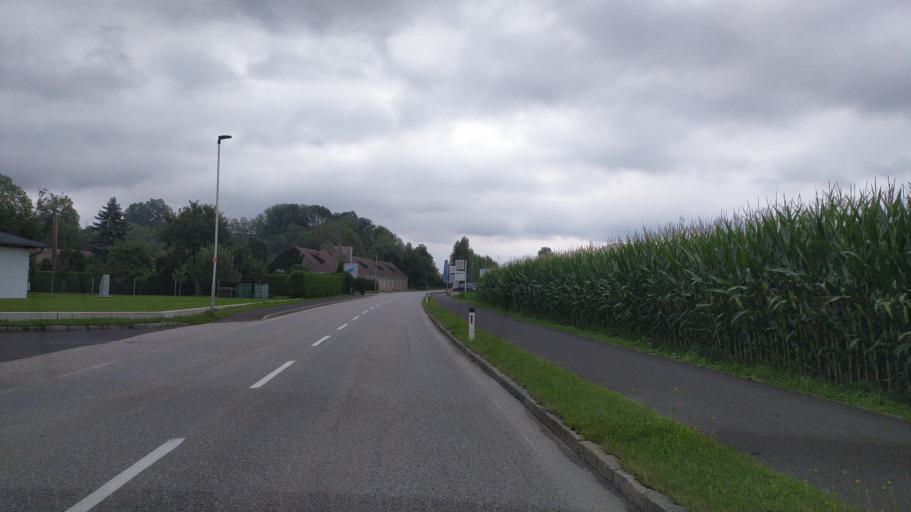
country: AT
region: Upper Austria
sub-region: Politischer Bezirk Linz-Land
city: Enns
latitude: 48.2555
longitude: 14.4658
